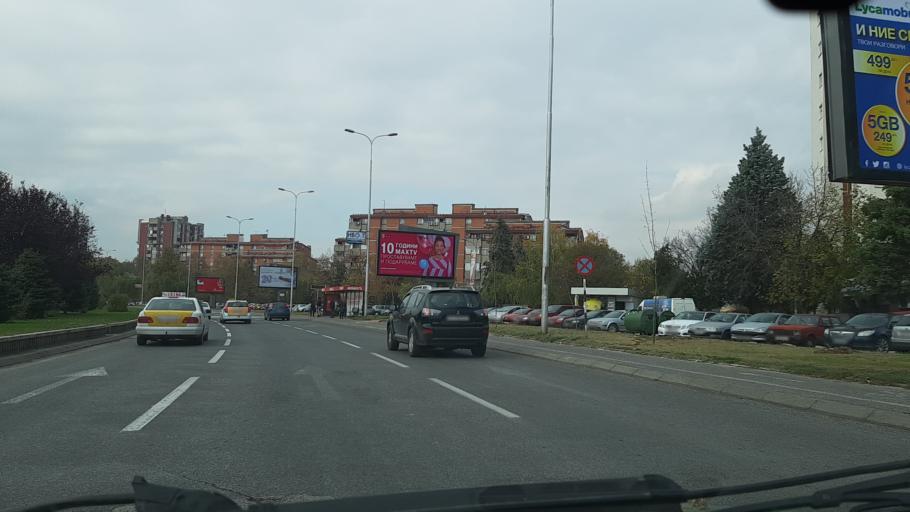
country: MK
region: Karpos
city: Skopje
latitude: 41.9893
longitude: 21.4590
